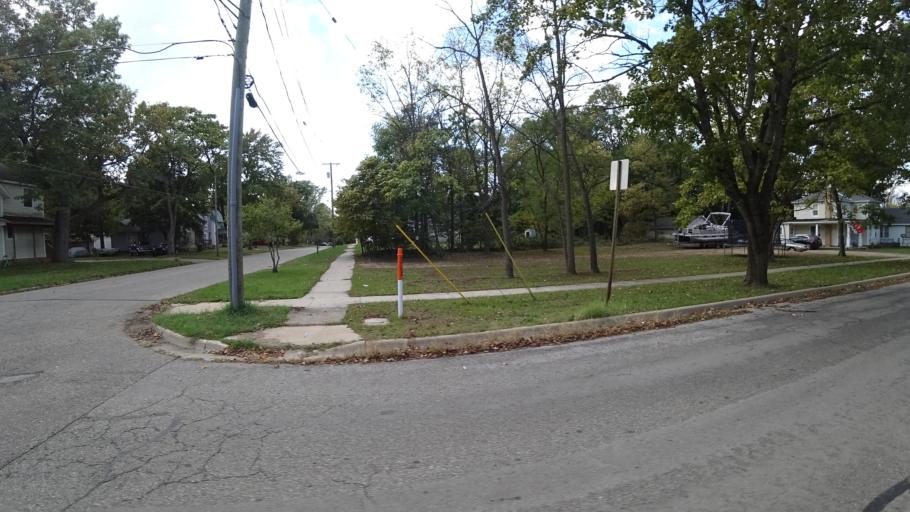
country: US
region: Michigan
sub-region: Saint Joseph County
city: Three Rivers
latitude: 41.9465
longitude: -85.6249
